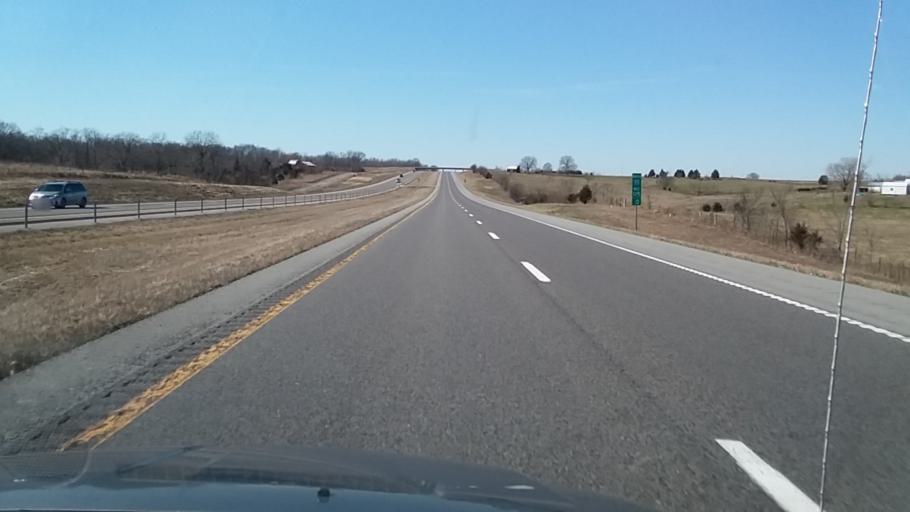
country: US
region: Missouri
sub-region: Cape Girardeau County
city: Jackson
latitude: 37.5426
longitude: -89.7261
